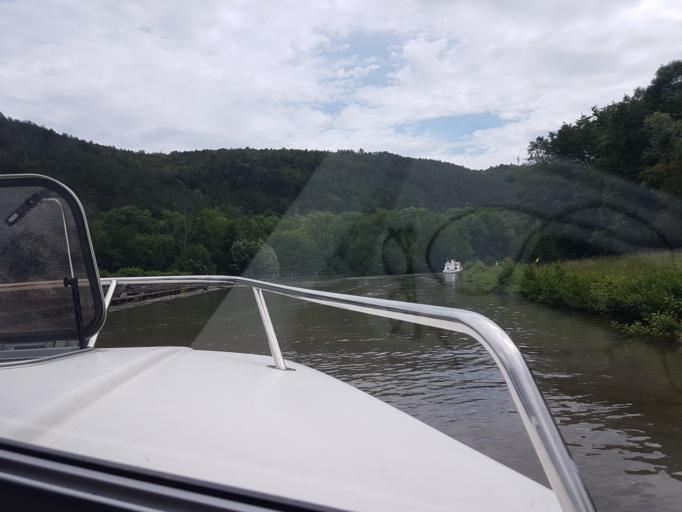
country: FR
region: Bourgogne
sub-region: Departement de la Nievre
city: Clamecy
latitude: 47.4771
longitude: 3.5250
